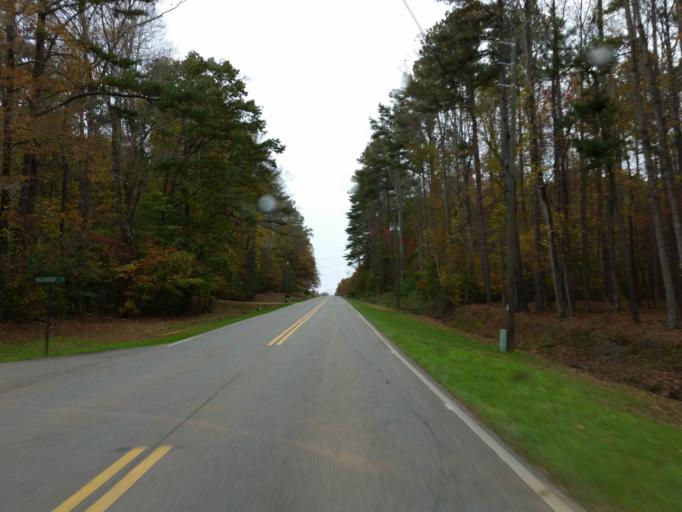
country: US
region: Georgia
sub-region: Pickens County
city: Jasper
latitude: 34.5023
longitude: -84.4362
